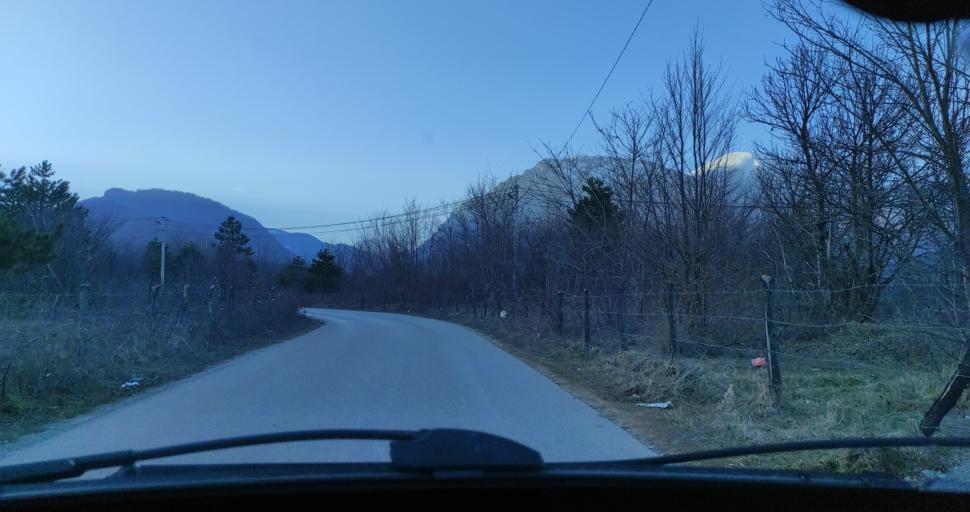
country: XK
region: Gjakova
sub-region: Komuna e Decanit
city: Decan
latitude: 42.5395
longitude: 20.2818
